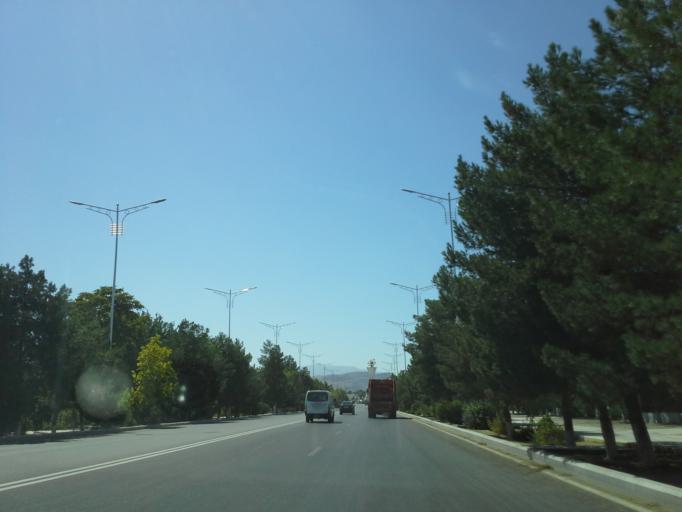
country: TM
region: Ahal
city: Ashgabat
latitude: 37.9302
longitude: 58.2996
